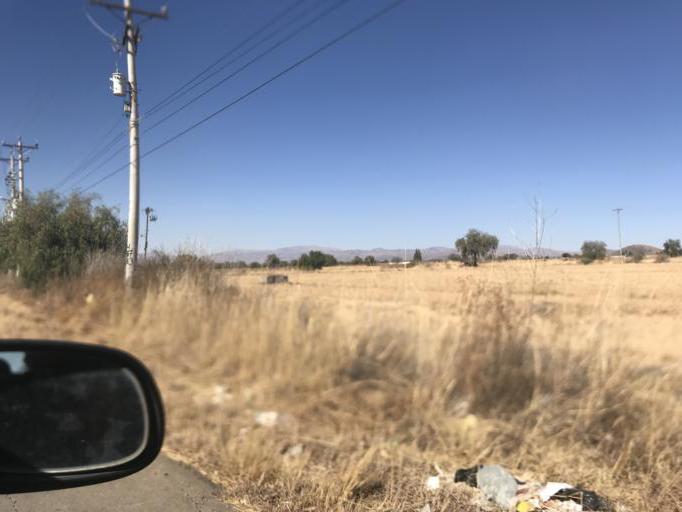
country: BO
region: Cochabamba
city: Tarata
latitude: -17.6066
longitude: -65.9972
